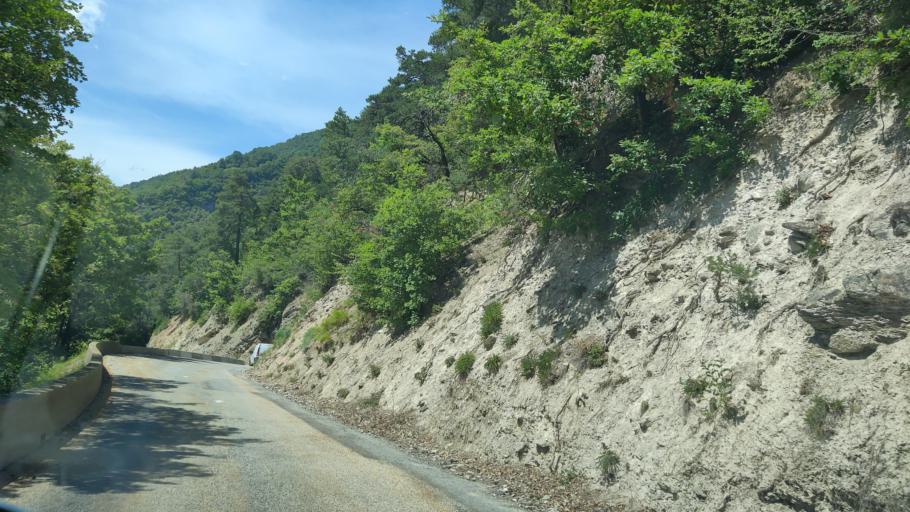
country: FR
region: Rhone-Alpes
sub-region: Departement de la Savoie
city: Salins-les-Thermes
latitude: 45.4628
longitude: 6.5535
